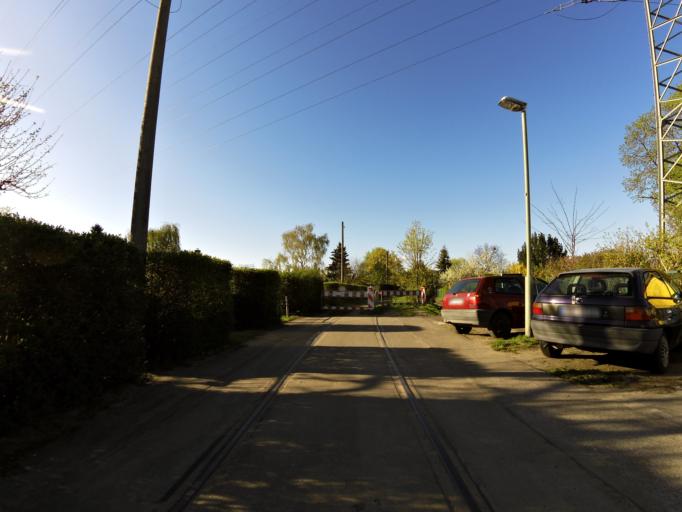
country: DE
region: Berlin
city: Baumschulenweg
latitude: 52.4723
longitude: 13.5006
